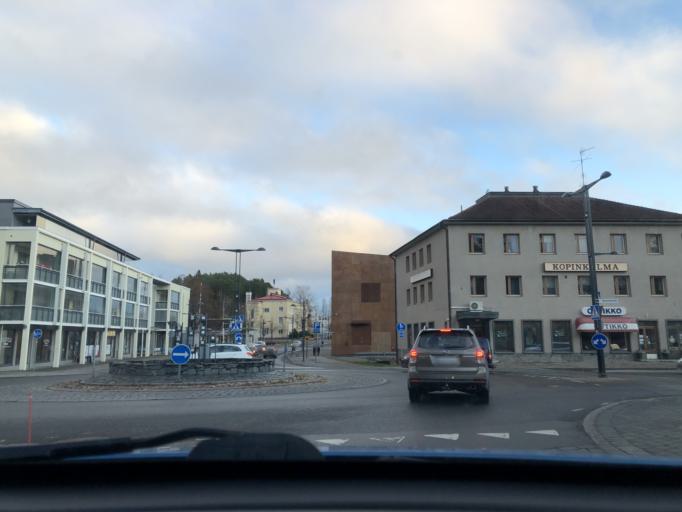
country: FI
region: Pirkanmaa
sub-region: Tampere
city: Kangasala
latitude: 61.4638
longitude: 24.0713
